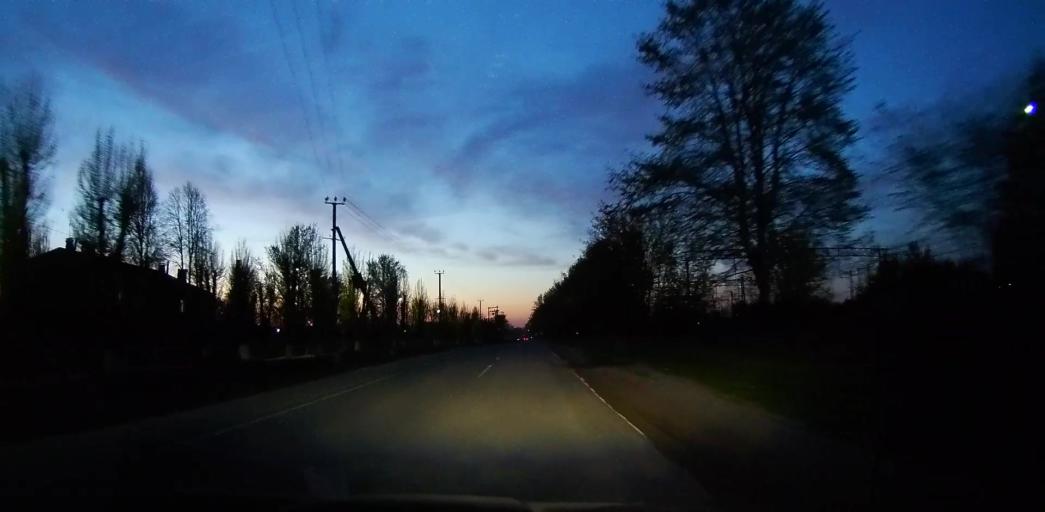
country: RU
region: Moskovskaya
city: Peski
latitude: 55.2110
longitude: 38.7724
